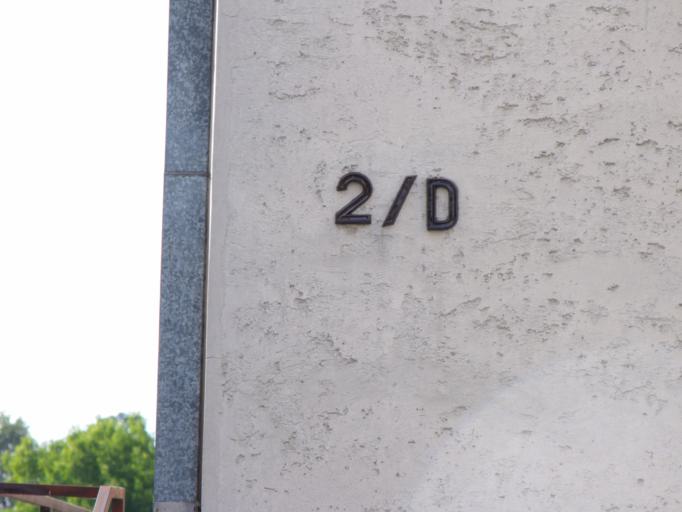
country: HU
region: Pest
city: Inarcs
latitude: 47.2561
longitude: 19.3320
